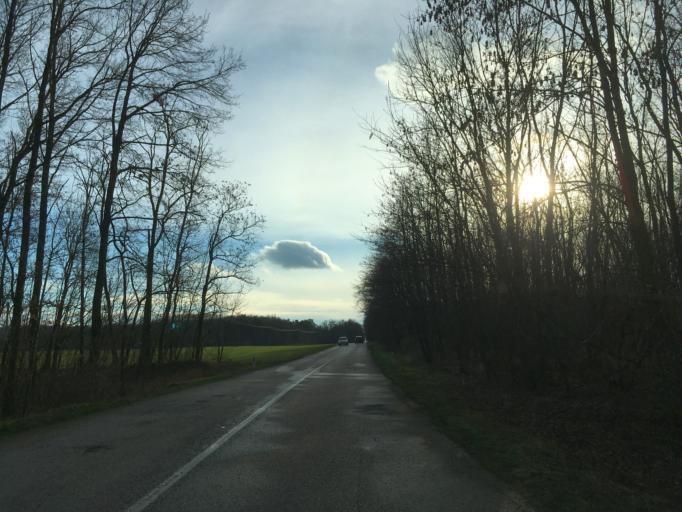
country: SK
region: Nitriansky
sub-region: Okres Nove Zamky
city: Nove Zamky
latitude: 47.9499
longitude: 18.2462
